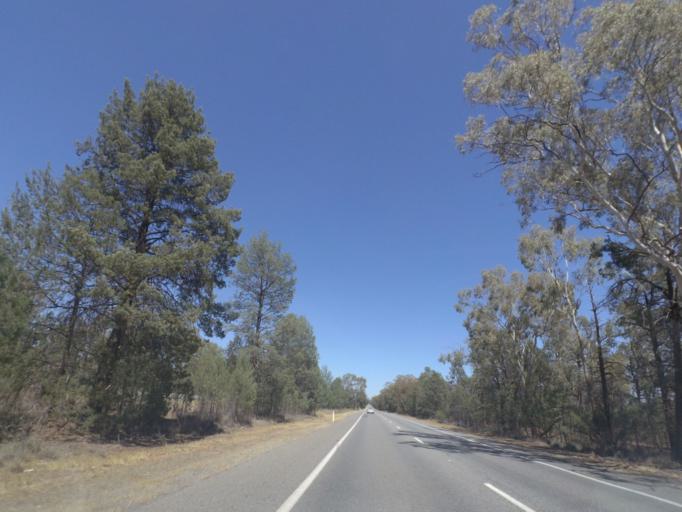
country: AU
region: New South Wales
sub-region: Narrandera
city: Narrandera
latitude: -34.7368
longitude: 146.5928
